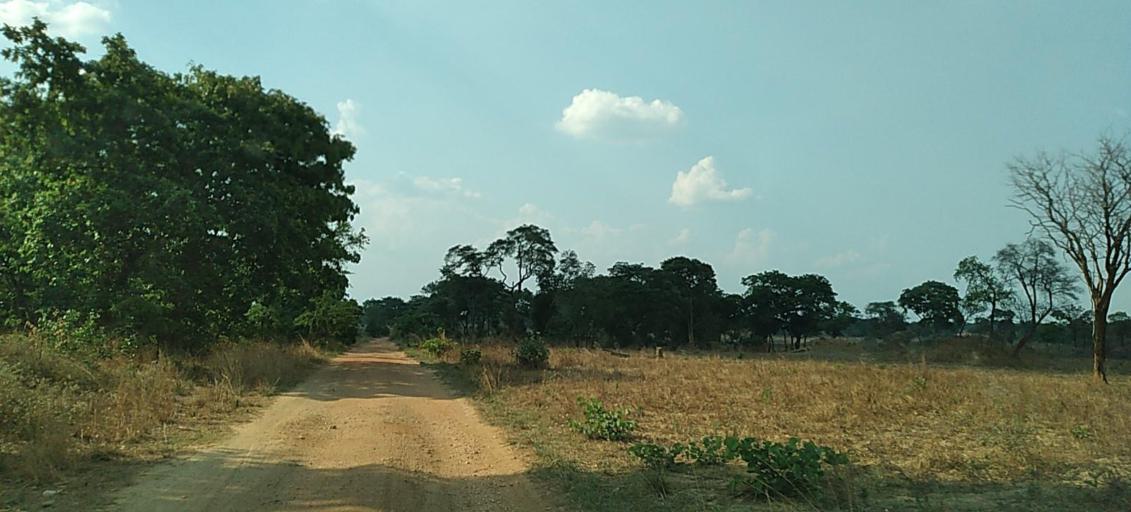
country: ZM
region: Copperbelt
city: Mpongwe
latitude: -13.5045
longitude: 28.0901
